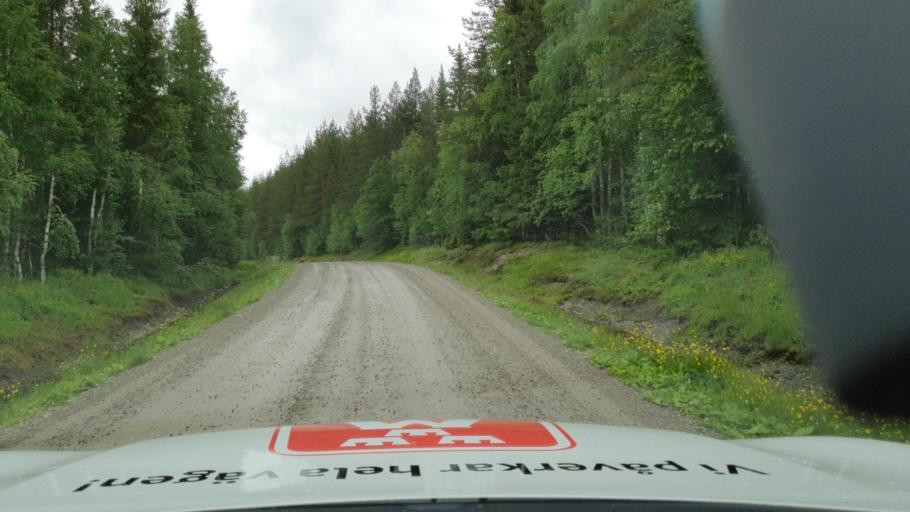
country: SE
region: Vaesterbotten
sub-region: Dorotea Kommun
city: Dorotea
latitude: 64.0415
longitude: 16.7508
